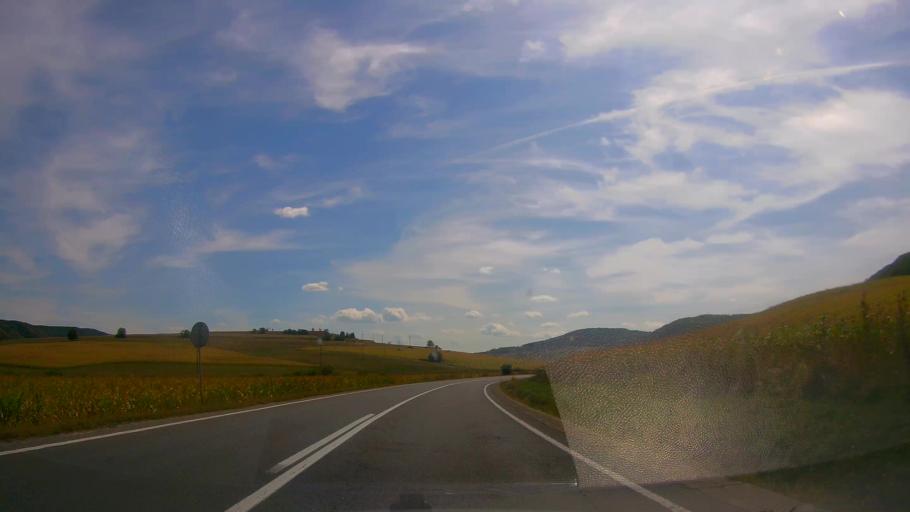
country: RO
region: Mures
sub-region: Comuna Nades
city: Nades
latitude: 46.3121
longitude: 24.7230
